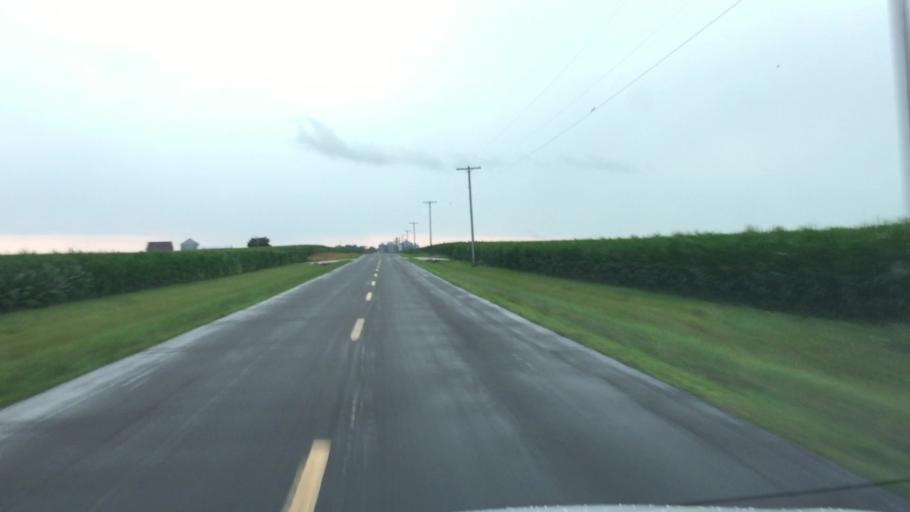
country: US
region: Illinois
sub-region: Hancock County
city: Carthage
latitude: 40.5200
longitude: -91.1417
